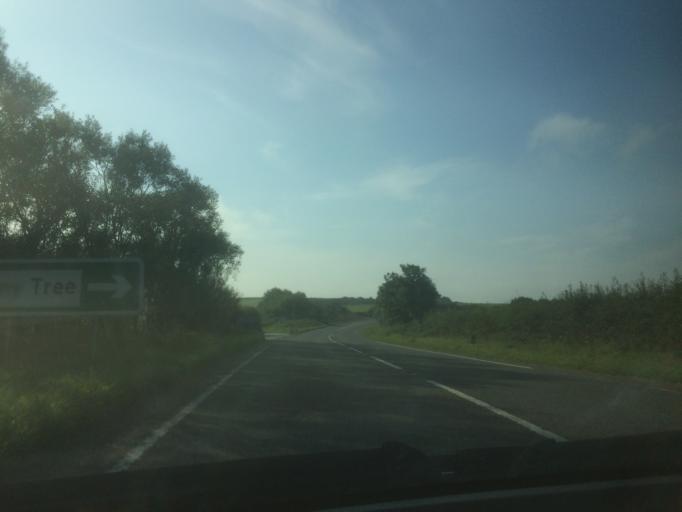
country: GB
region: England
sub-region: Cornwall
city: Callington
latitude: 50.4901
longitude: -4.2887
